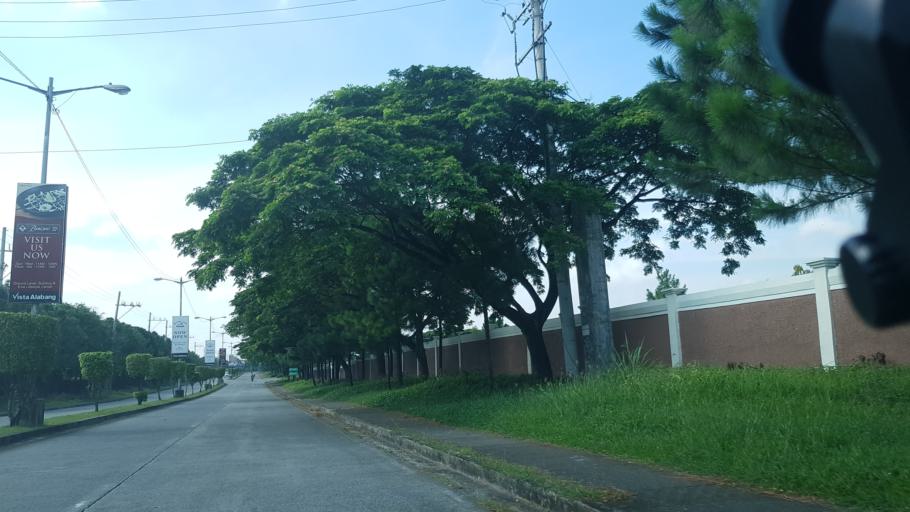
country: PH
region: Calabarzon
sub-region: Province of Laguna
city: Magsaysay
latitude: 14.3610
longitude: 121.0095
